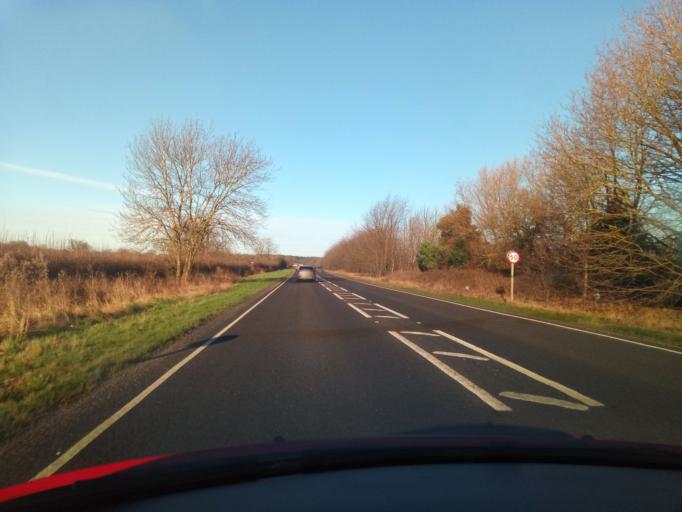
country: GB
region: England
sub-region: Nottinghamshire
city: Farnsfield
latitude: 53.0455
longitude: -1.0615
